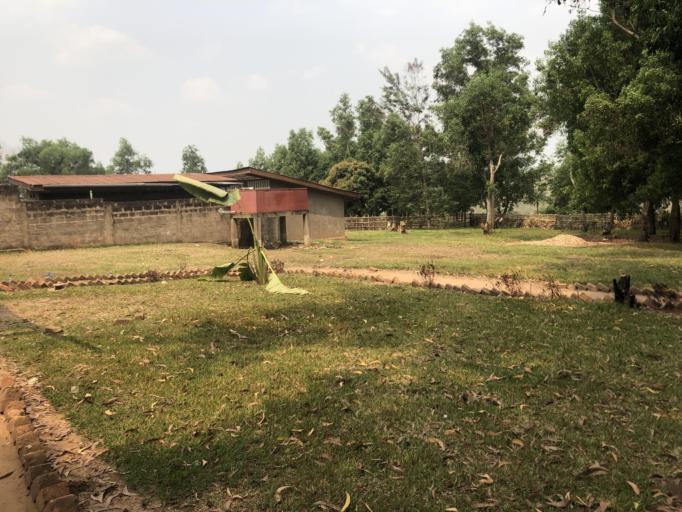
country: CD
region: Bandundu
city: Kikwit
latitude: -5.0722
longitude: 18.8473
